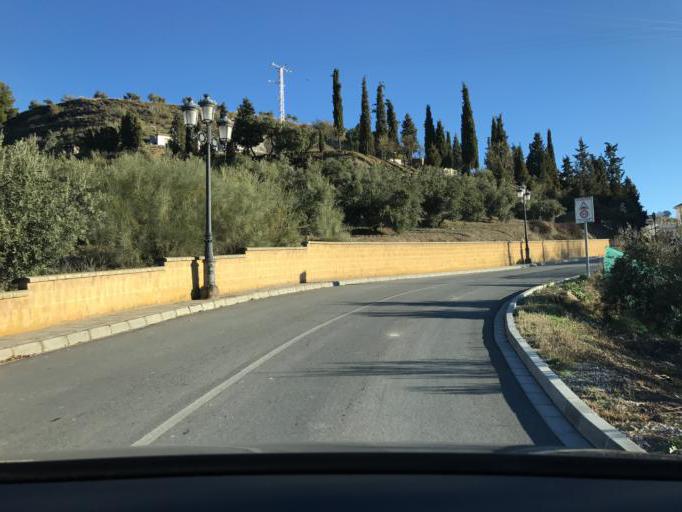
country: ES
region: Andalusia
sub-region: Provincia de Granada
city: Calicasas
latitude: 37.2722
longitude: -3.6256
